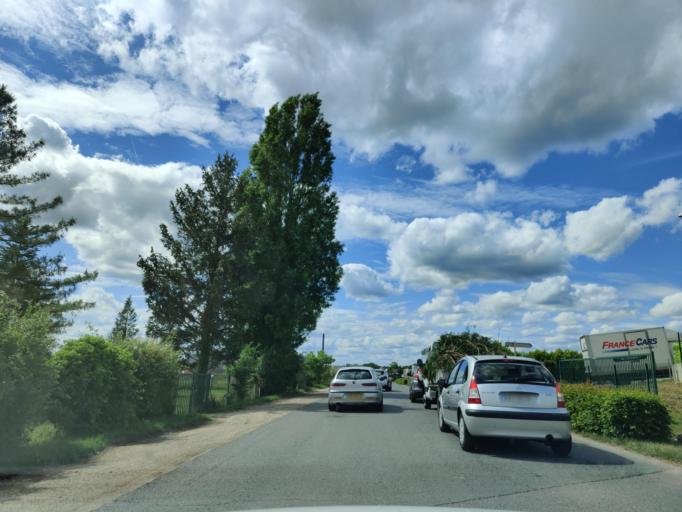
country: FR
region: Ile-de-France
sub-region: Departement de l'Essonne
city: Egly
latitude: 48.5716
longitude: 2.2094
